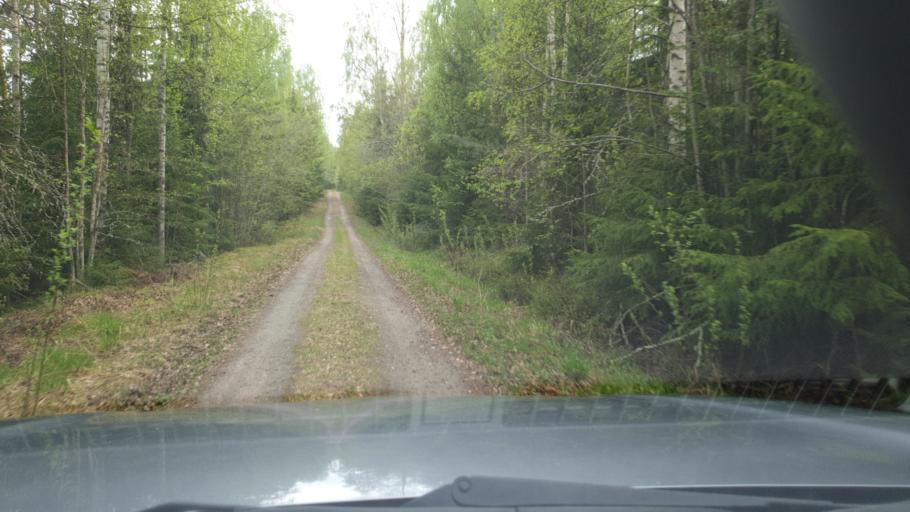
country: SE
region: Gaevleborg
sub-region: Ljusdals Kommun
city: Jaervsoe
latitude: 61.6475
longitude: 16.3087
